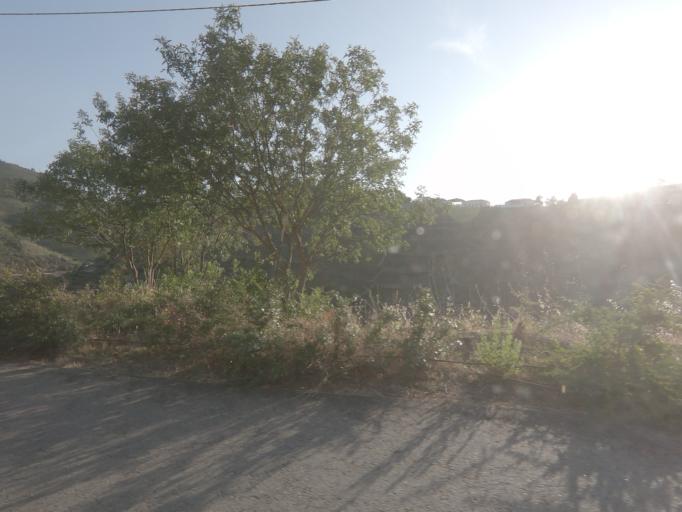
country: PT
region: Vila Real
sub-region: Sabrosa
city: Vilela
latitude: 41.1641
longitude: -7.6243
